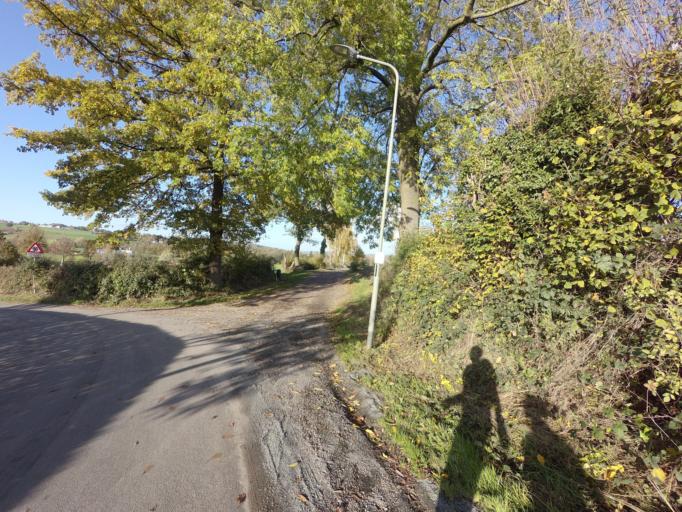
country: BE
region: Wallonia
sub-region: Province de Liege
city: Plombieres
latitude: 50.7645
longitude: 5.9178
